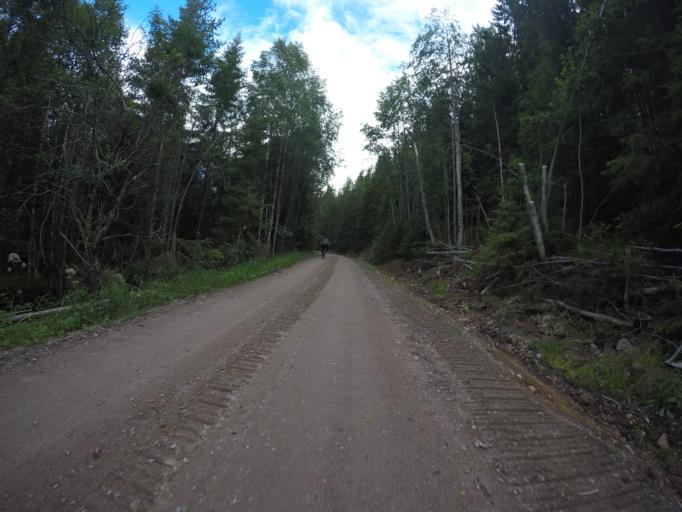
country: SE
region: Vaermland
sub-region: Filipstads Kommun
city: Lesjofors
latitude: 60.0102
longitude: 14.4085
